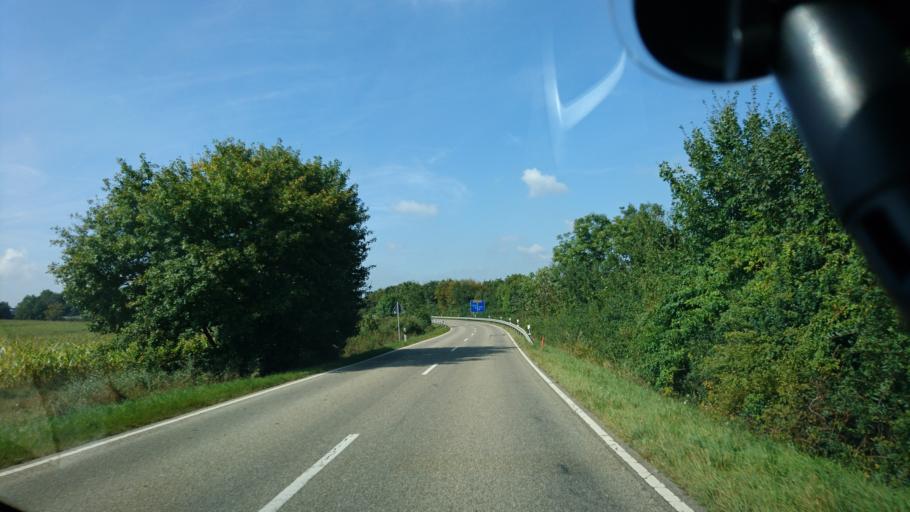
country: DE
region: Baden-Wuerttemberg
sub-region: Regierungsbezirk Stuttgart
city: Wolpertshausen
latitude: 49.1763
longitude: 9.8693
